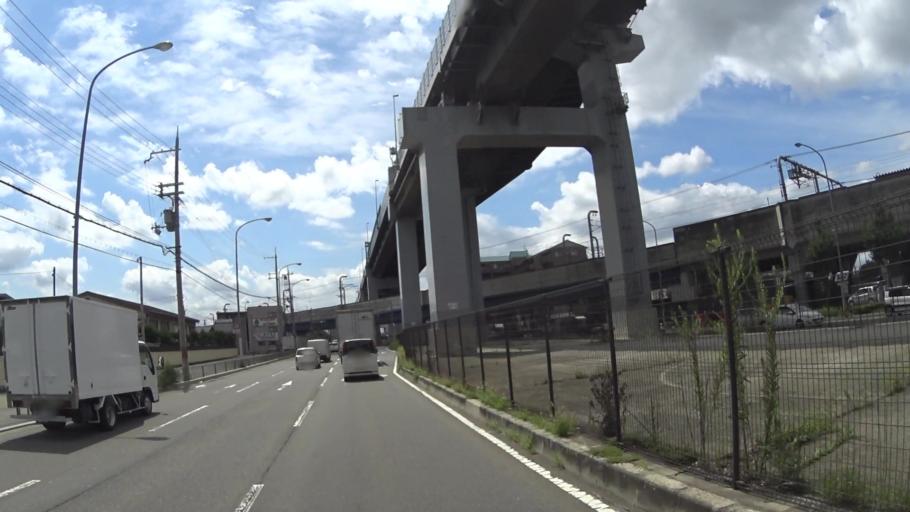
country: JP
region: Kyoto
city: Muko
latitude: 34.9655
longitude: 135.7532
